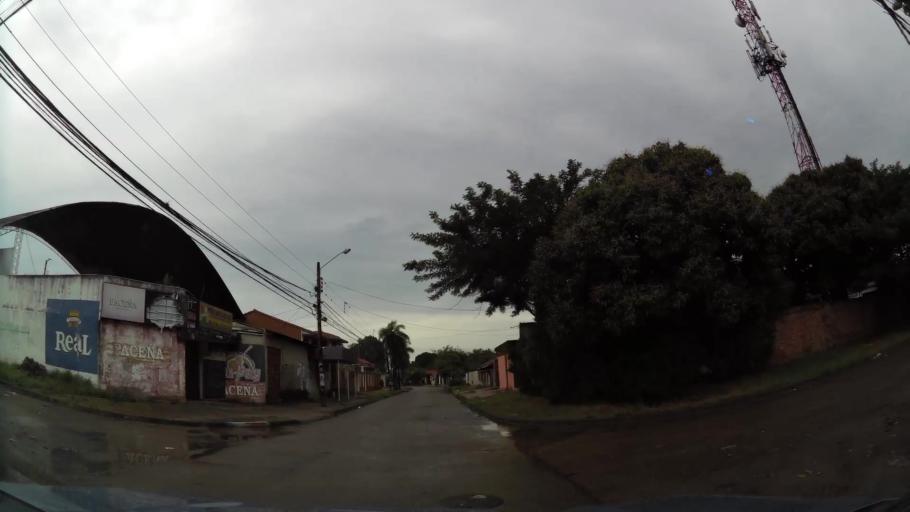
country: BO
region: Santa Cruz
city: Santa Cruz de la Sierra
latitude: -17.8057
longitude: -63.1855
